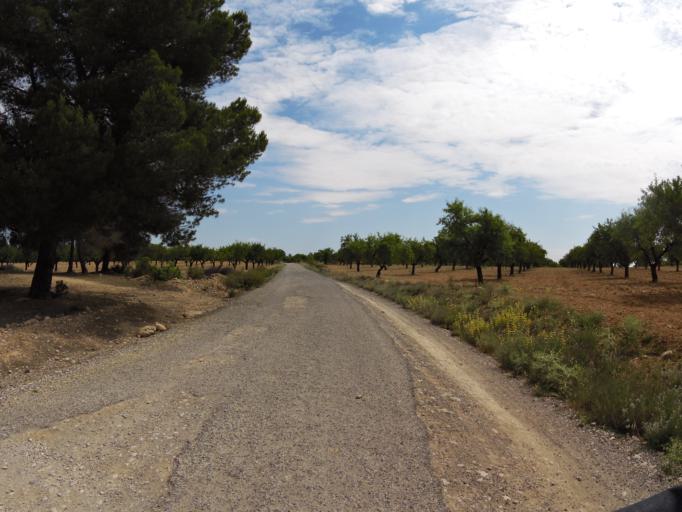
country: ES
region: Castille-La Mancha
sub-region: Provincia de Albacete
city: Casas Ibanez
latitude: 39.3551
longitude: -1.4753
